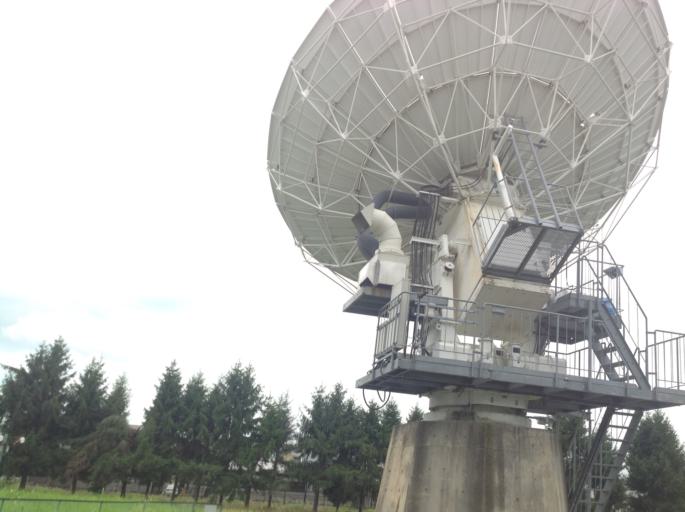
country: JP
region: Iwate
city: Mizusawa
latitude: 39.1335
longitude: 141.1324
